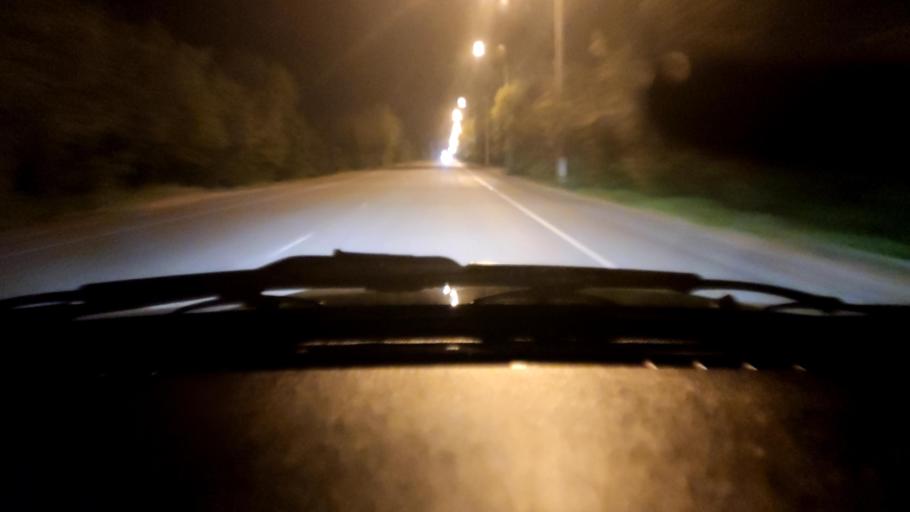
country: RU
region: Voronezj
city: Shilovo
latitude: 51.5763
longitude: 39.1478
